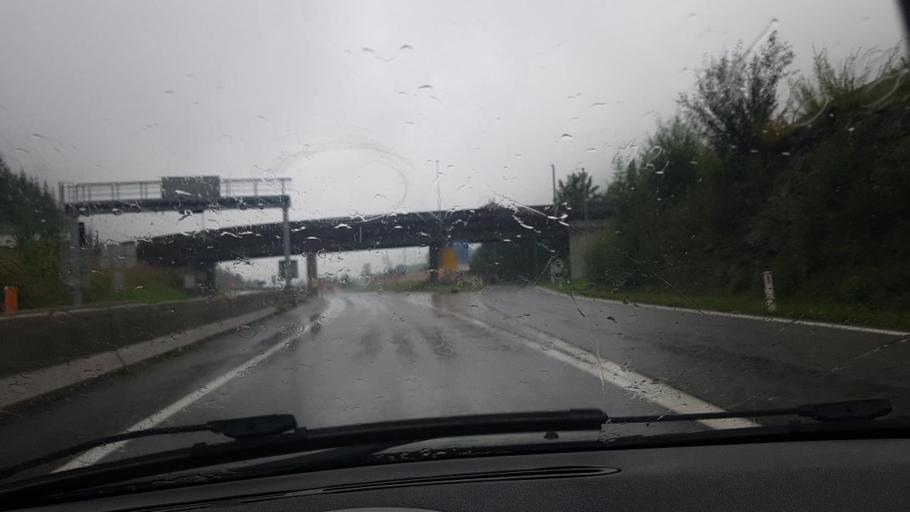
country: AT
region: Vorarlberg
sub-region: Politischer Bezirk Bludenz
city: Klosterle
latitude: 47.1306
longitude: 10.1155
